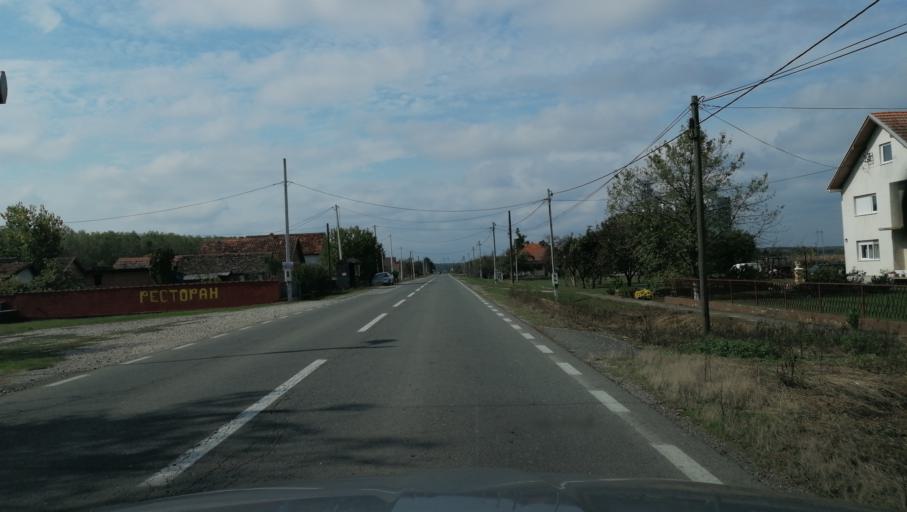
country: RS
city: Bosut
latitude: 44.9244
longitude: 19.3403
